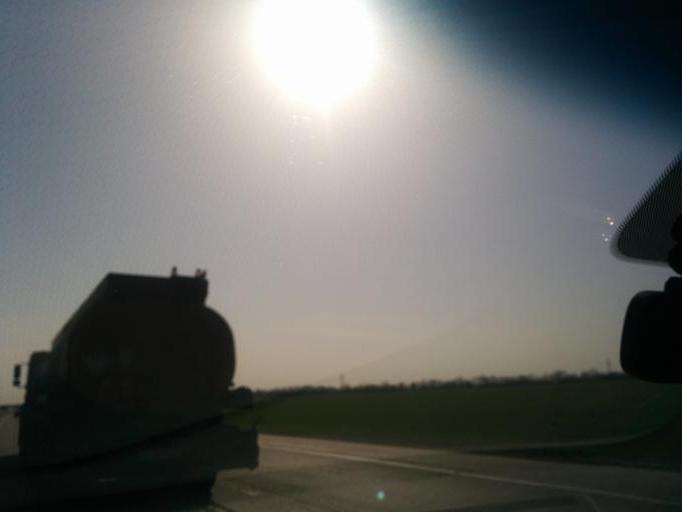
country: RU
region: Rostov
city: Mayskiy
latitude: 47.6816
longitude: 40.0723
